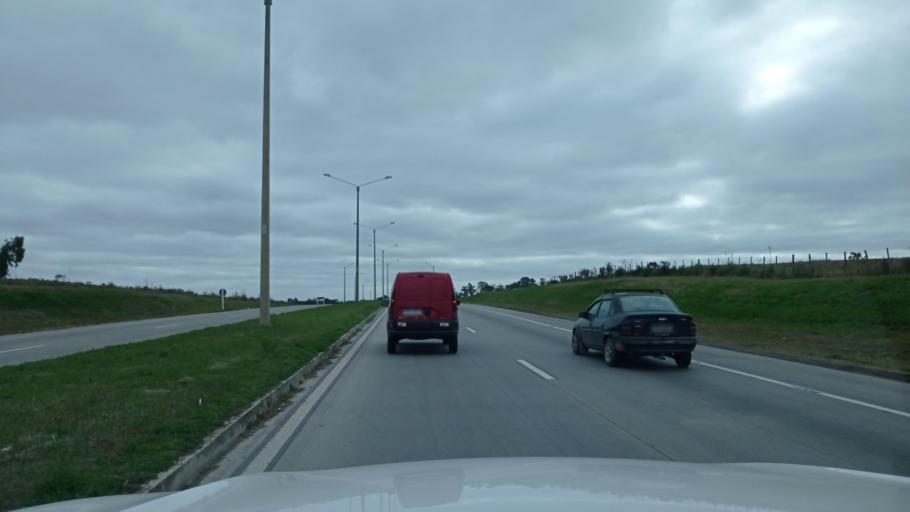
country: UY
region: Canelones
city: Toledo
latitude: -34.7914
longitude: -56.1031
